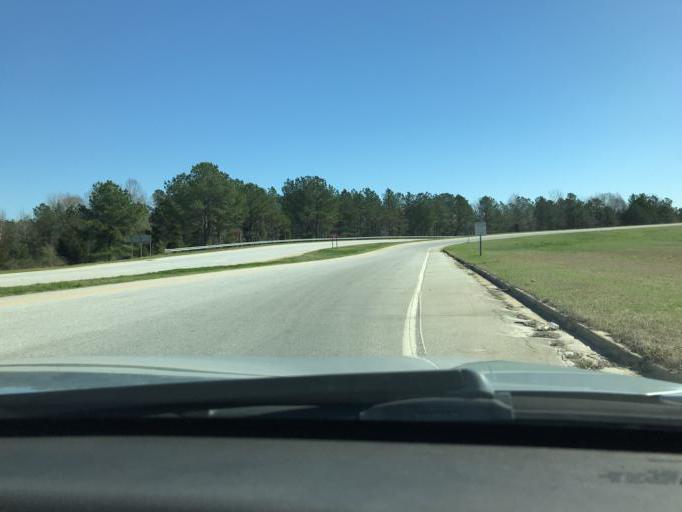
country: US
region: South Carolina
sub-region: Laurens County
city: Watts Mills
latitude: 34.5543
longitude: -82.0064
